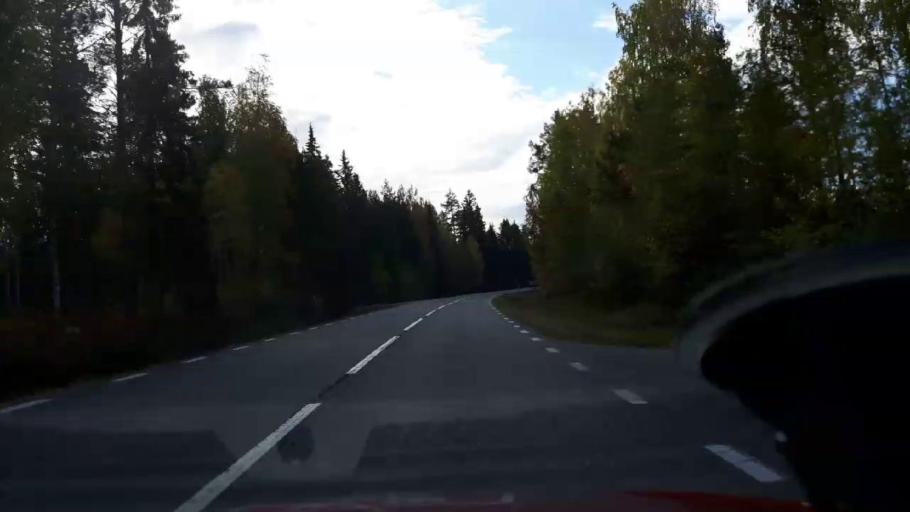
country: SE
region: Gaevleborg
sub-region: Ljusdals Kommun
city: Farila
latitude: 62.0150
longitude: 15.2399
